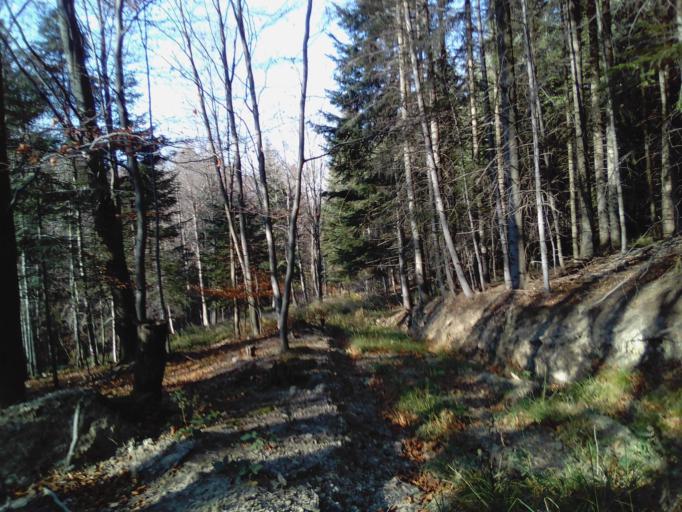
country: PL
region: Subcarpathian Voivodeship
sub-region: Powiat strzyzowski
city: Wisniowa
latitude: 49.8467
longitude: 21.6657
